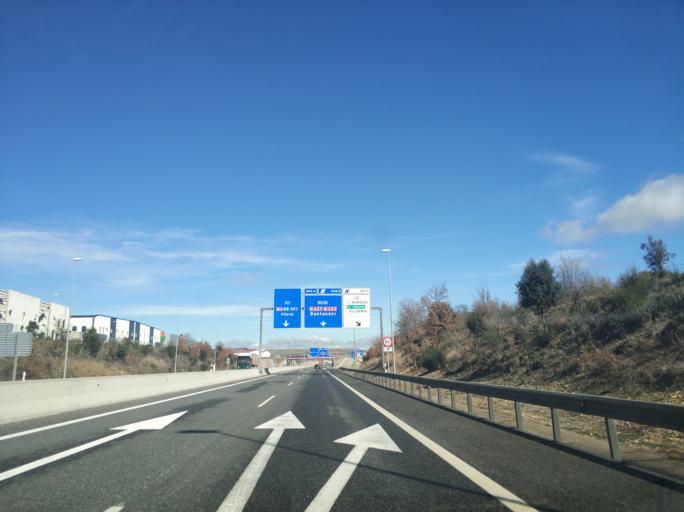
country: ES
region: Castille and Leon
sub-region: Provincia de Burgos
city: Cardenajimeno
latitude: 42.3570
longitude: -3.6382
